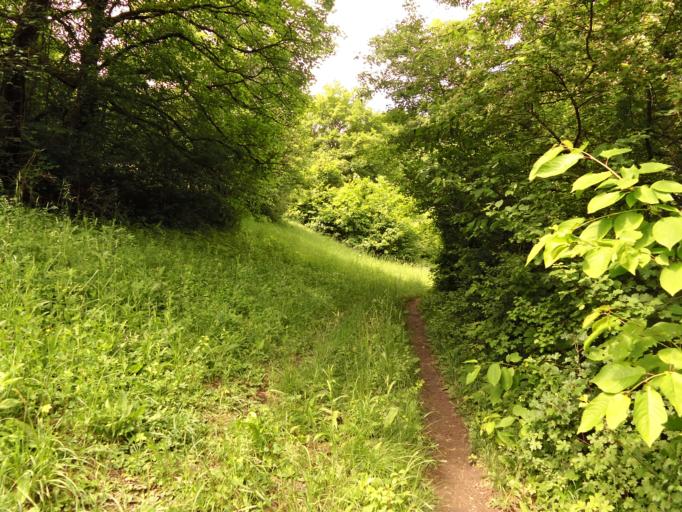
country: DE
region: Bavaria
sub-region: Regierungsbezirk Unterfranken
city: Hochberg
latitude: 49.7934
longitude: 9.8881
